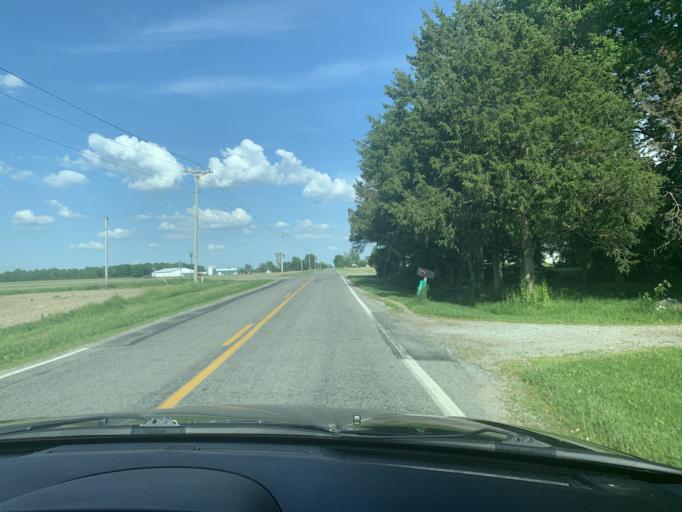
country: US
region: Ohio
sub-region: Logan County
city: De Graff
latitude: 40.2431
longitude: -83.9971
